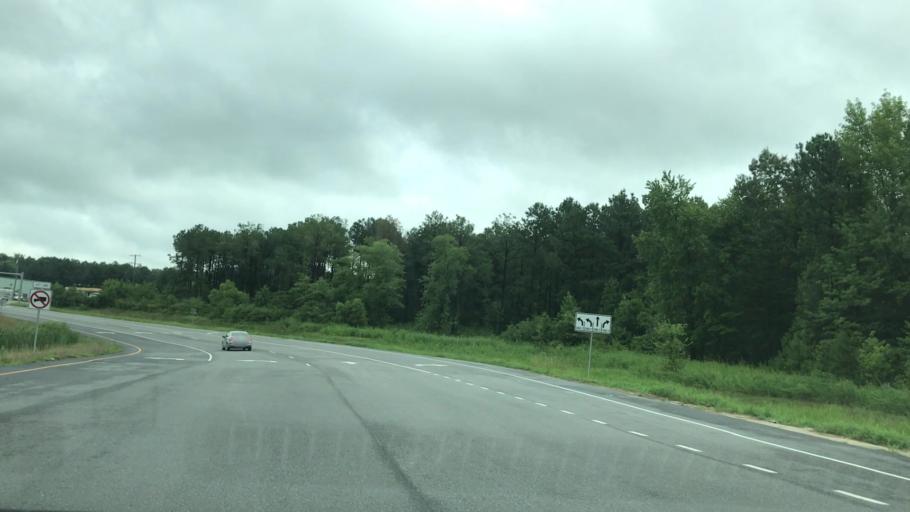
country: US
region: Virginia
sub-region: Hanover County
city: Ashland
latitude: 37.7211
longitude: -77.4467
